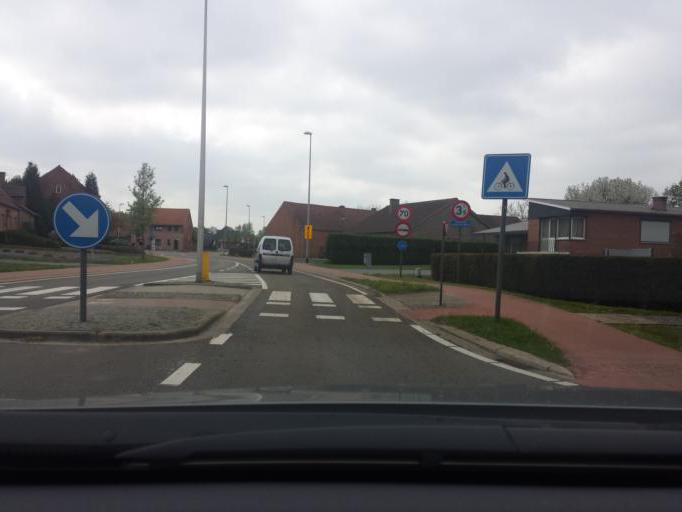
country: BE
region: Flanders
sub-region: Provincie Limburg
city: Lummen
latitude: 51.0147
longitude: 5.2033
